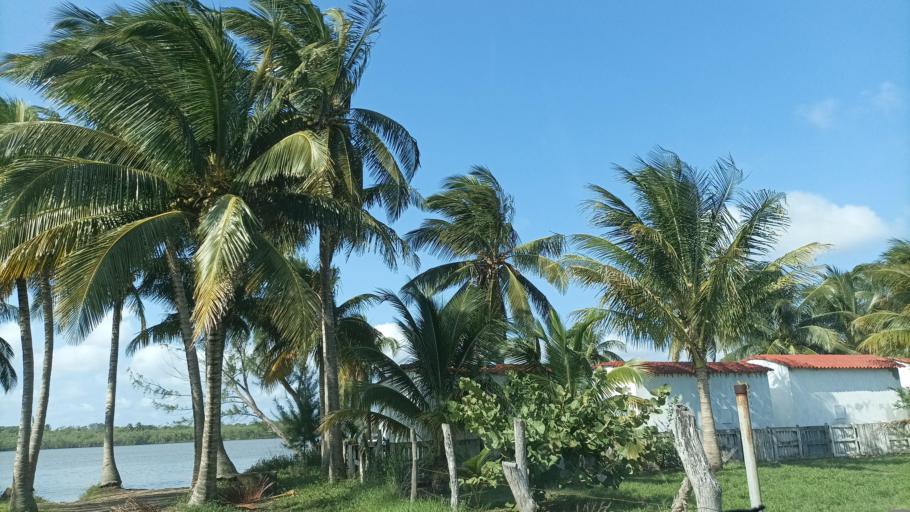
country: MX
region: Veracruz
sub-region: Coatzacoalcos
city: Fraccionamiento Ciudad Olmeca
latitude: 18.2069
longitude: -94.6093
